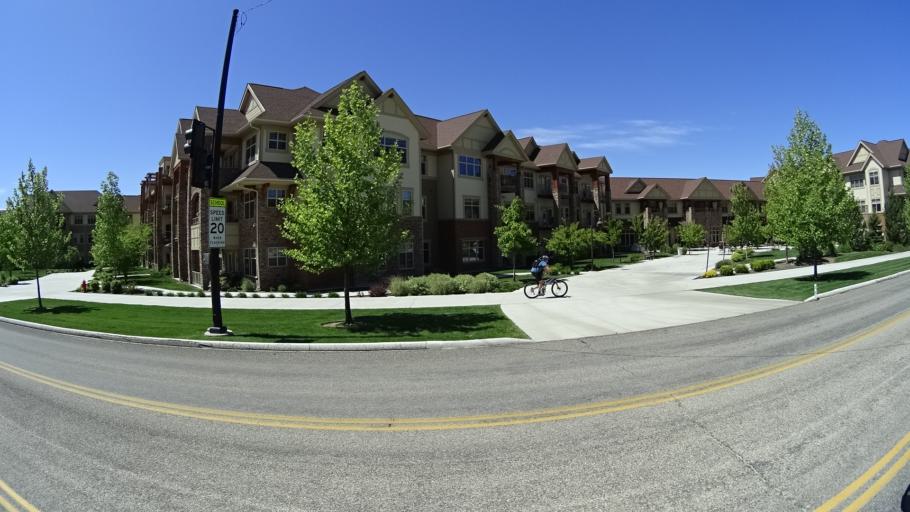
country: US
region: Idaho
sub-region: Ada County
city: Boise
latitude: 43.5668
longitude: -116.1168
